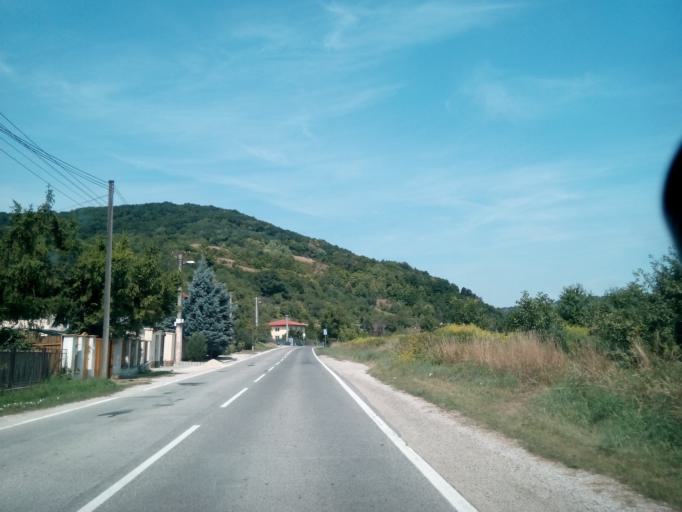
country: SK
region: Kosicky
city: Kosice
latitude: 48.7530
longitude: 21.2483
